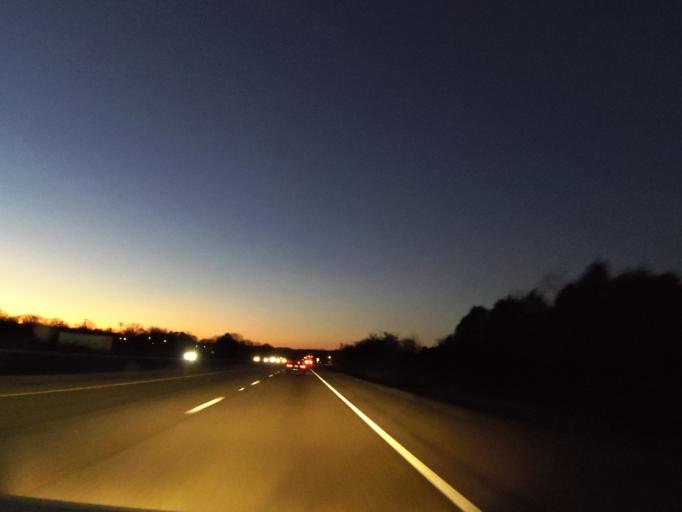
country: US
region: Tennessee
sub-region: Jefferson County
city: White Pine
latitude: 36.0318
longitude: -83.3180
